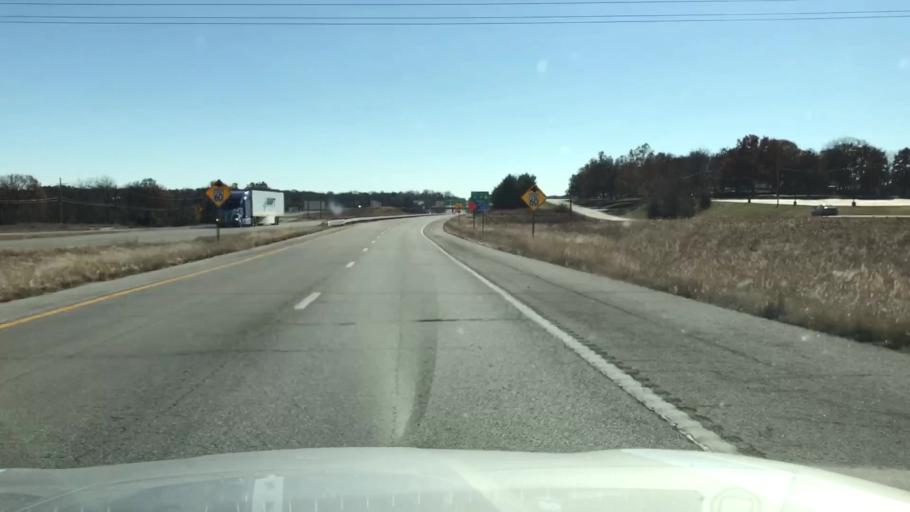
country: US
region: Missouri
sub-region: Jasper County
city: Carthage
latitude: 37.0897
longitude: -94.3124
